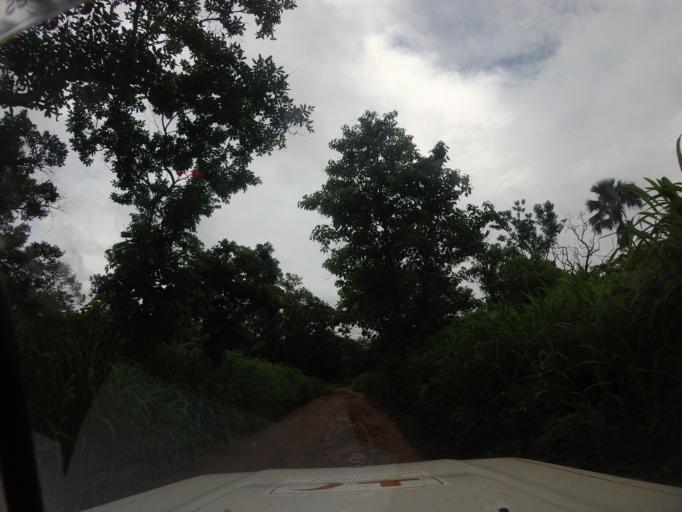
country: SL
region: Northern Province
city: Kamakwie
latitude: 9.6504
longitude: -12.2194
